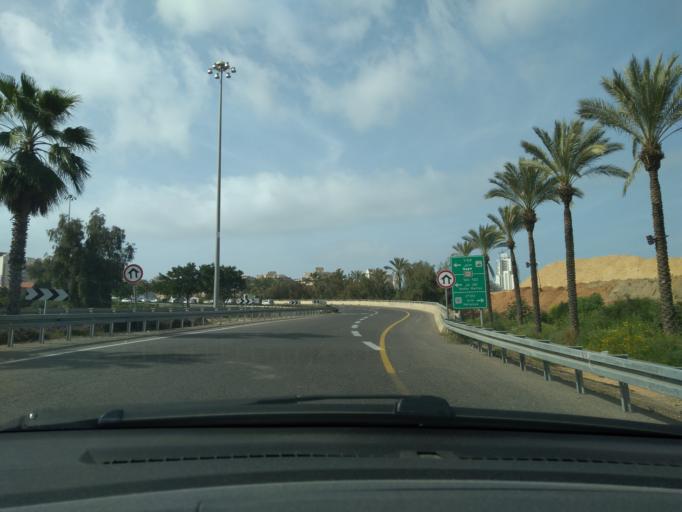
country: IL
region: Central District
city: Even Yehuda
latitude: 32.2885
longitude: 34.8592
